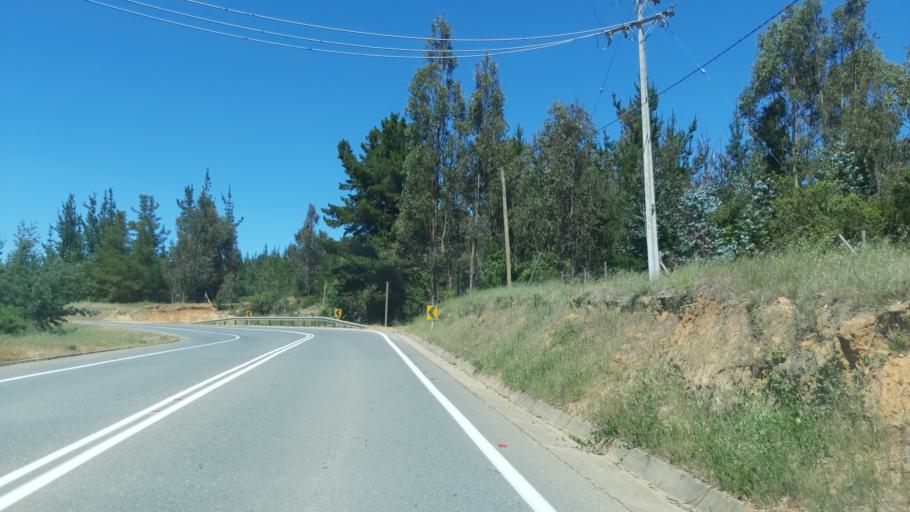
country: CL
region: Maule
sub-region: Provincia de Talca
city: Talca
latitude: -34.9657
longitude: -71.9640
